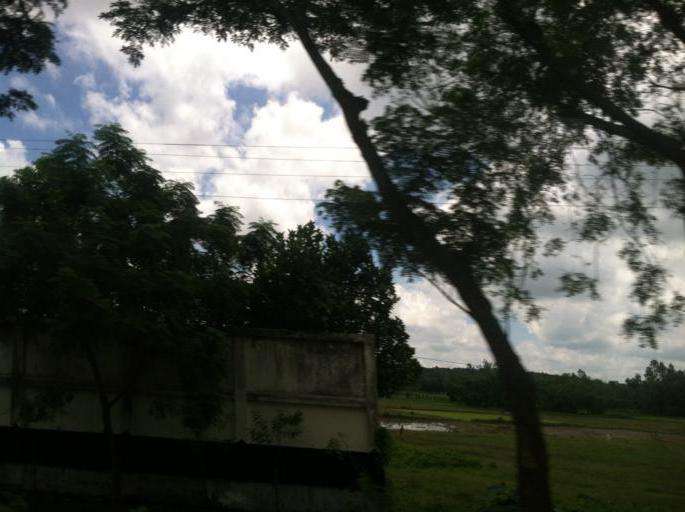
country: BD
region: Sylhet
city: Habiganj
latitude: 24.2098
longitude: 91.3554
